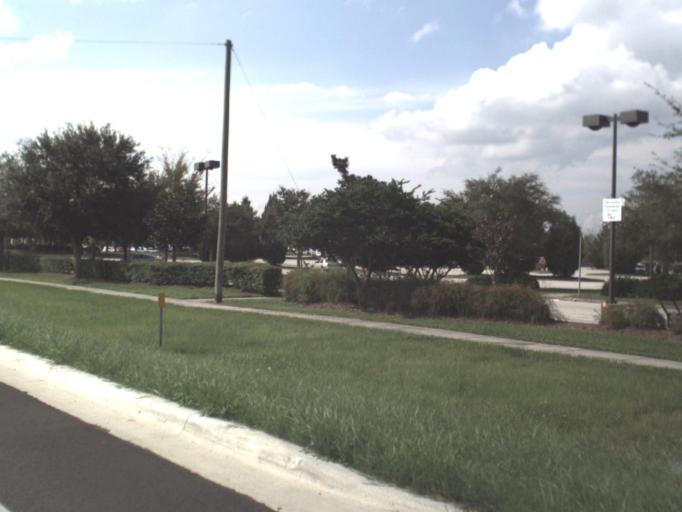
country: US
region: Florida
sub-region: Manatee County
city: Ellenton
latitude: 27.4934
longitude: -82.4831
